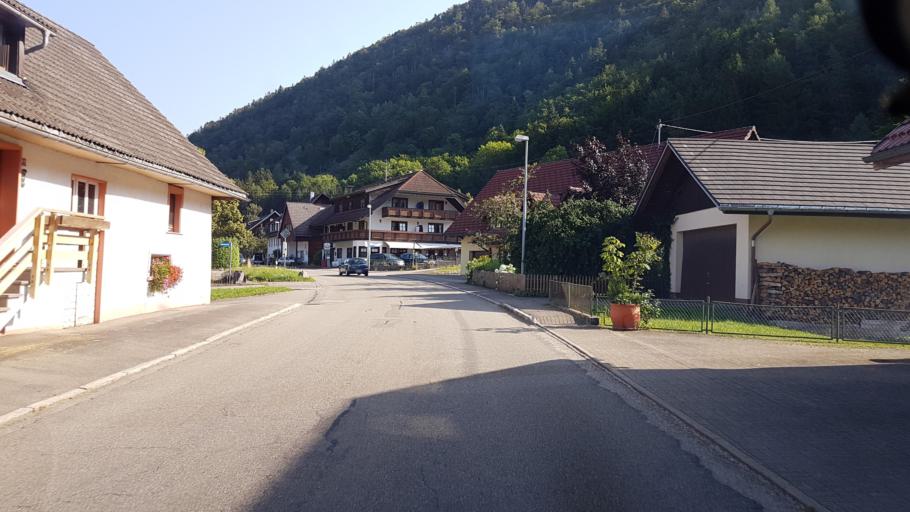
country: DE
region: Baden-Wuerttemberg
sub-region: Freiburg Region
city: Dachsberg
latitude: 47.6965
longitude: 8.1252
